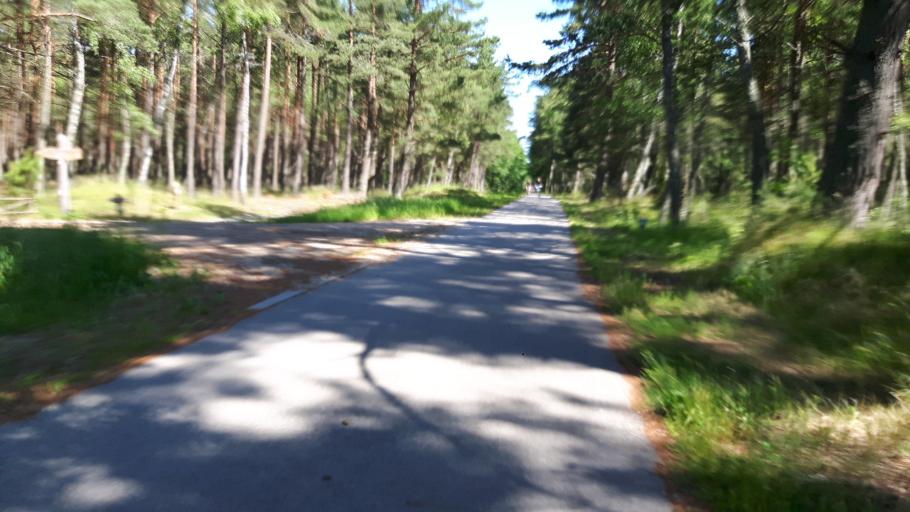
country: LT
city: Neringa
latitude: 55.3510
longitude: 21.0462
